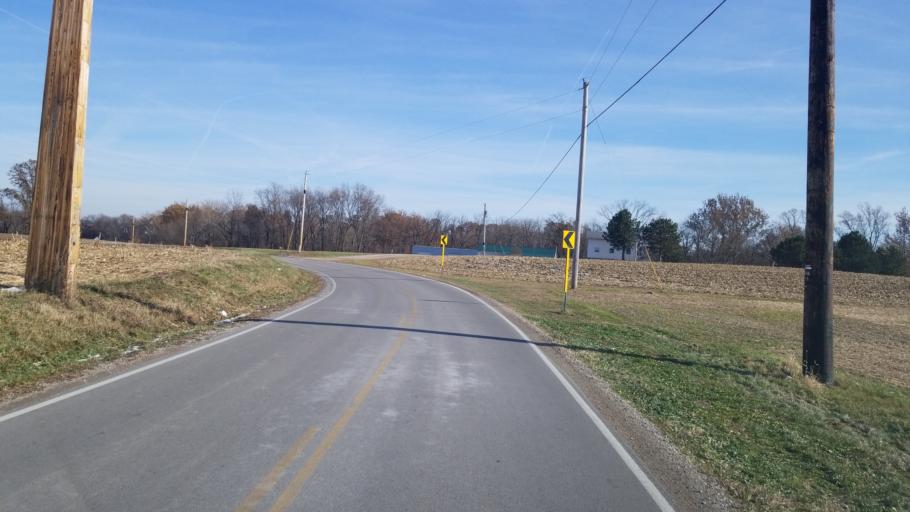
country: US
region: Ohio
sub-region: Huron County
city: Monroeville
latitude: 41.1945
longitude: -82.6784
